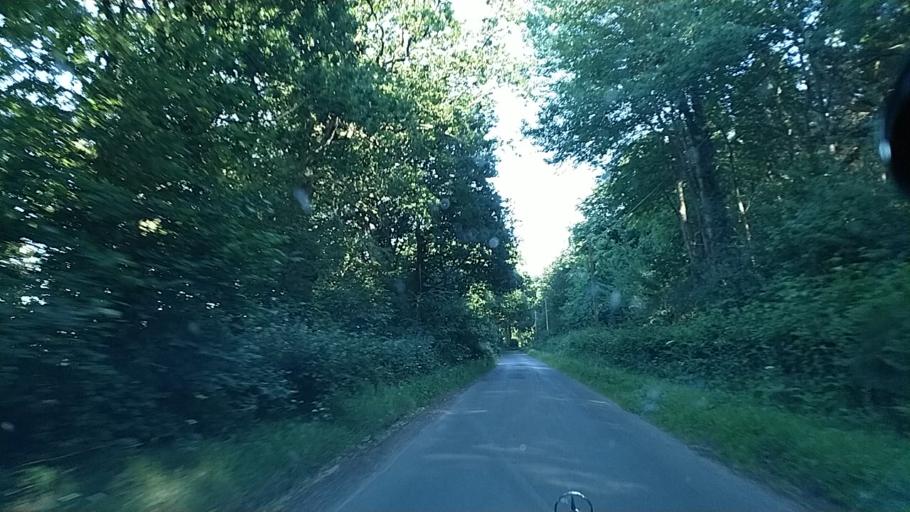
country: GB
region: England
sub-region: Warwickshire
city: Wroxall
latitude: 52.3435
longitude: -1.6509
